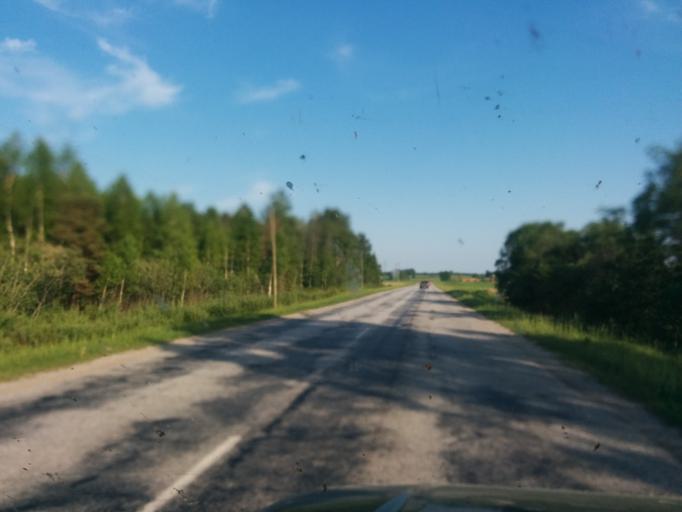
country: LV
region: Talsu Rajons
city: Talsi
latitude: 57.2996
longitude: 22.5584
